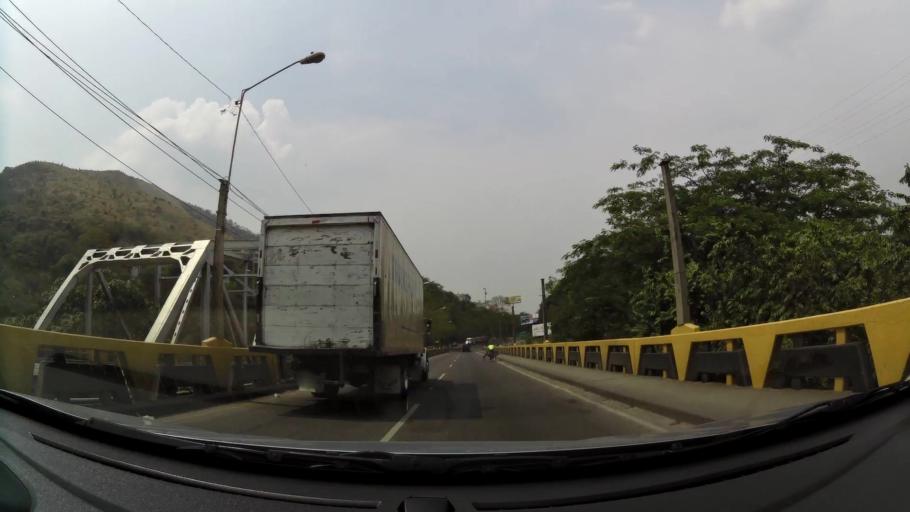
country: HN
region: Cortes
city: El Maranon
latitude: 15.4282
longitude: -88.0231
